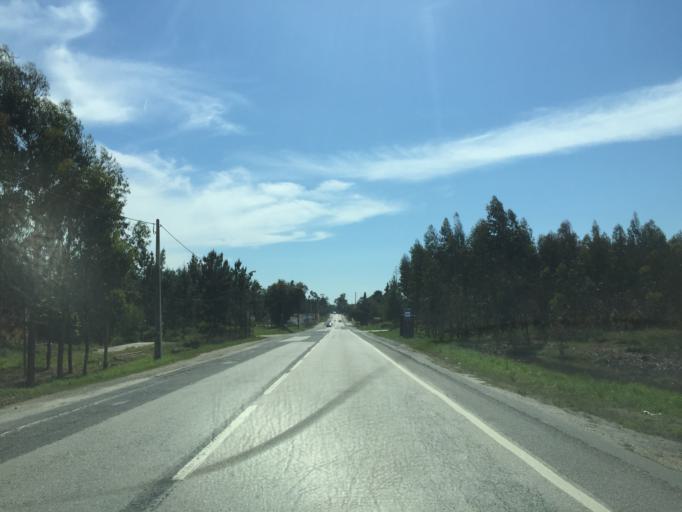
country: PT
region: Coimbra
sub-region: Soure
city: Soure
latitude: 39.9977
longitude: -8.5999
